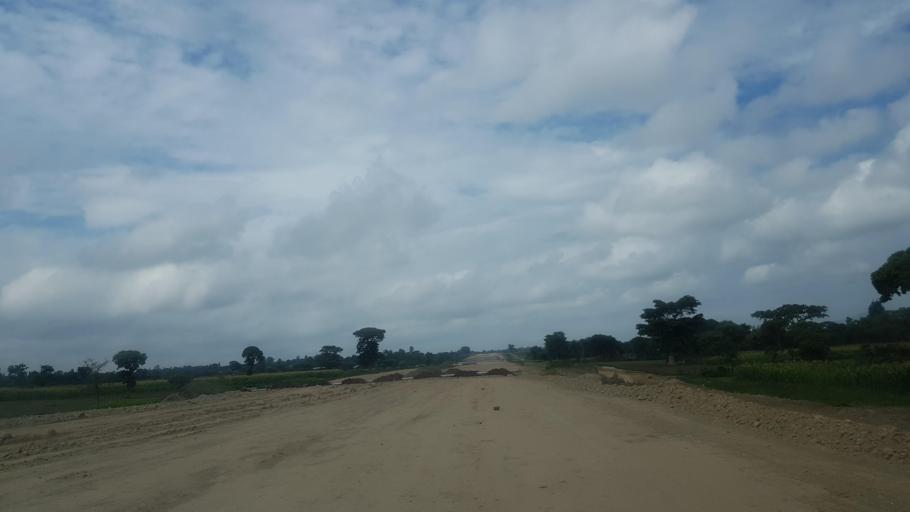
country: ET
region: Oromiya
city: Shashemene
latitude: 7.2838
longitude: 38.6075
